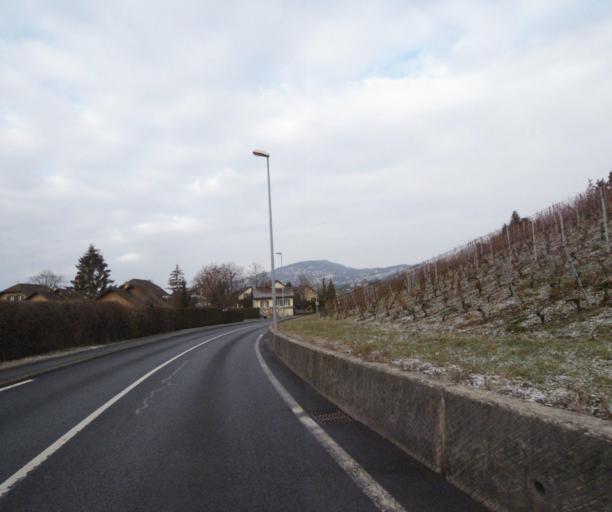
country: CH
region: Vaud
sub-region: Riviera-Pays-d'Enhaut District
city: La Tour-de-Peilz
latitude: 46.4600
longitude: 6.8725
